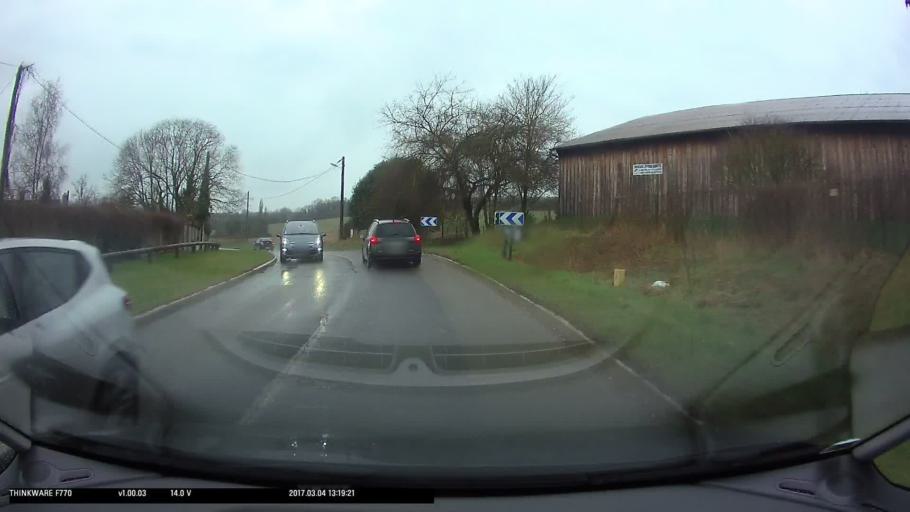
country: FR
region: Ile-de-France
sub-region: Departement du Val-d'Oise
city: Ableiges
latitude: 49.0973
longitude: 1.9776
